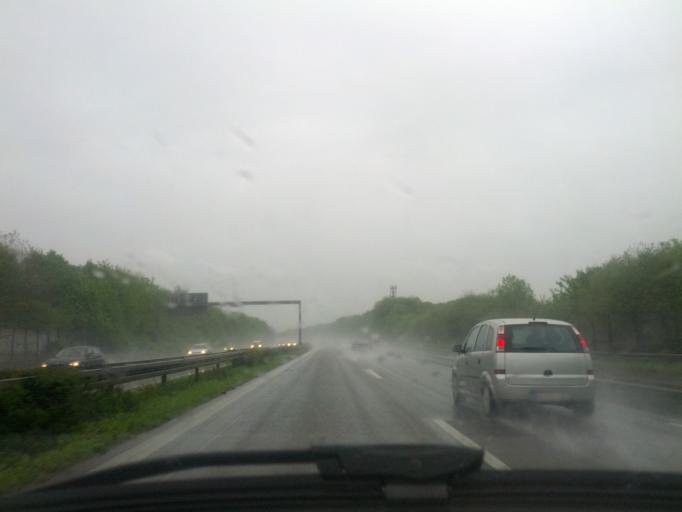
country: DE
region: North Rhine-Westphalia
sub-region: Regierungsbezirk Koln
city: Neustadt/Sued
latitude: 50.8904
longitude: 6.9271
